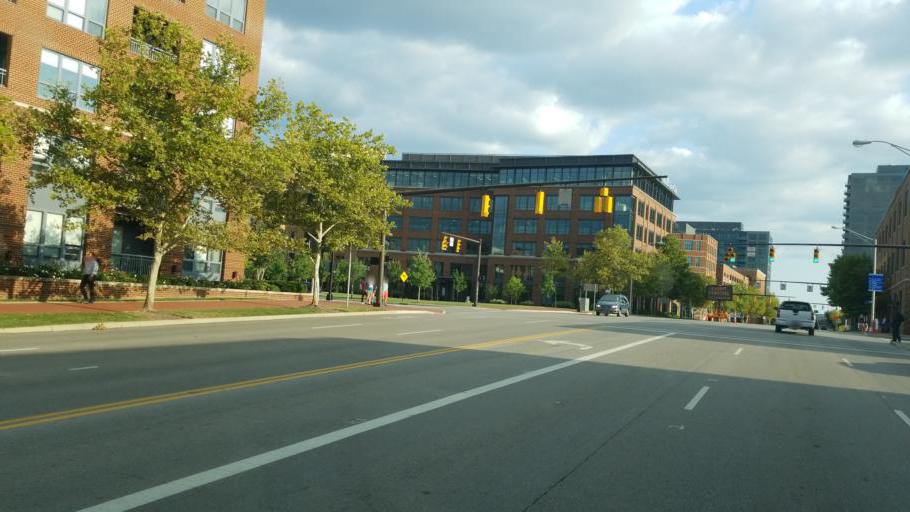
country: US
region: Ohio
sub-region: Franklin County
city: Columbus
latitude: 39.9698
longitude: -83.0096
